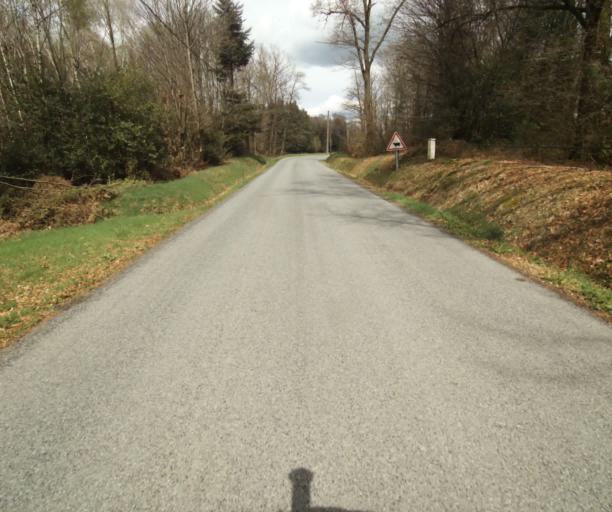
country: FR
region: Limousin
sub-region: Departement de la Correze
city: Argentat
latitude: 45.2048
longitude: 1.8949
